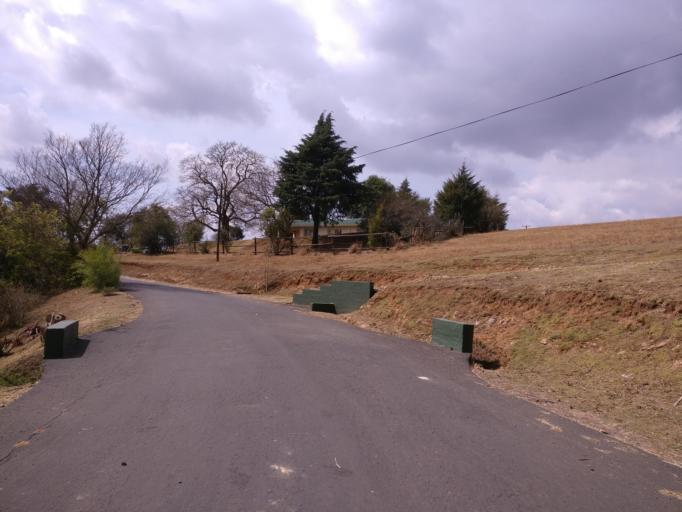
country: ZA
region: KwaZulu-Natal
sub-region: uThukela District Municipality
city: Bergville
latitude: -29.0146
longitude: 29.4190
